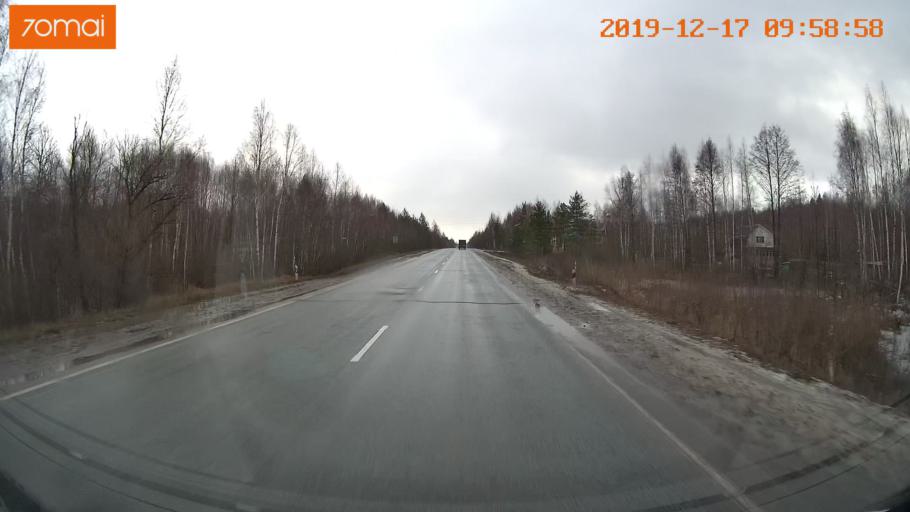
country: RU
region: Vladimir
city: Golovino
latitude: 55.9625
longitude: 40.5571
